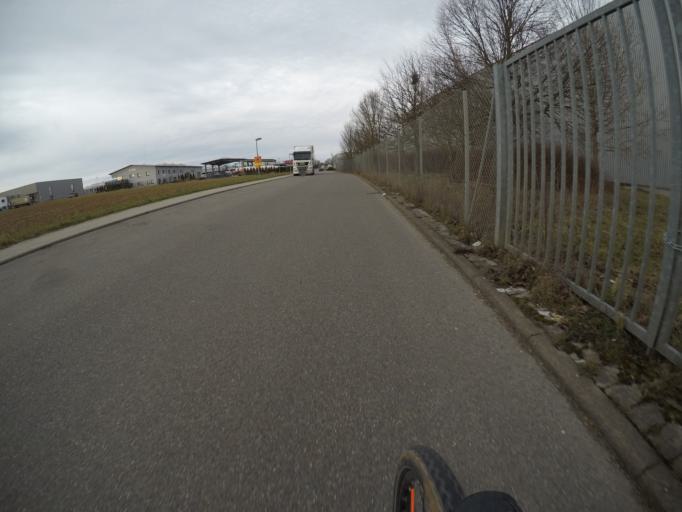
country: DE
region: Baden-Wuerttemberg
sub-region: Regierungsbezirk Stuttgart
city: Nufringen
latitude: 48.6302
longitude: 8.8983
